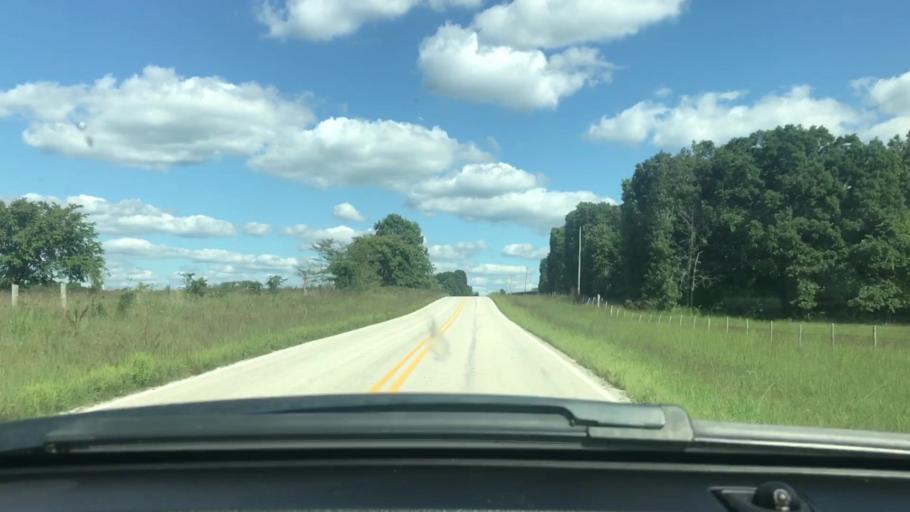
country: US
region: Missouri
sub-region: Wright County
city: Hartville
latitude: 37.3769
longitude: -92.4124
